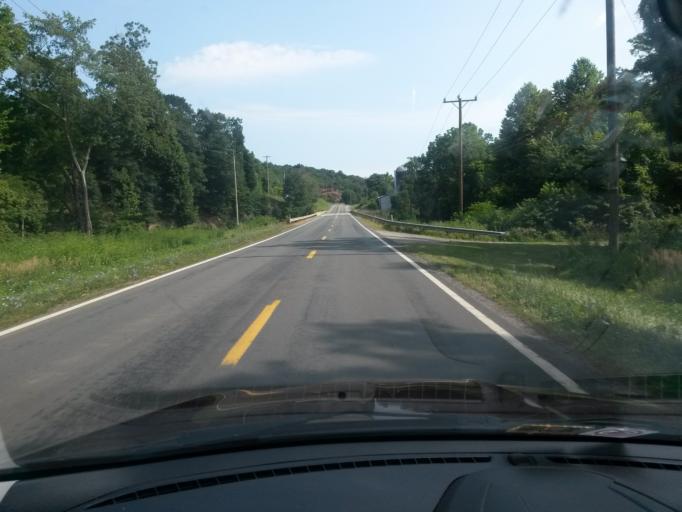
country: US
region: Virginia
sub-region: Shenandoah County
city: Basye
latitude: 38.9611
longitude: -78.8042
